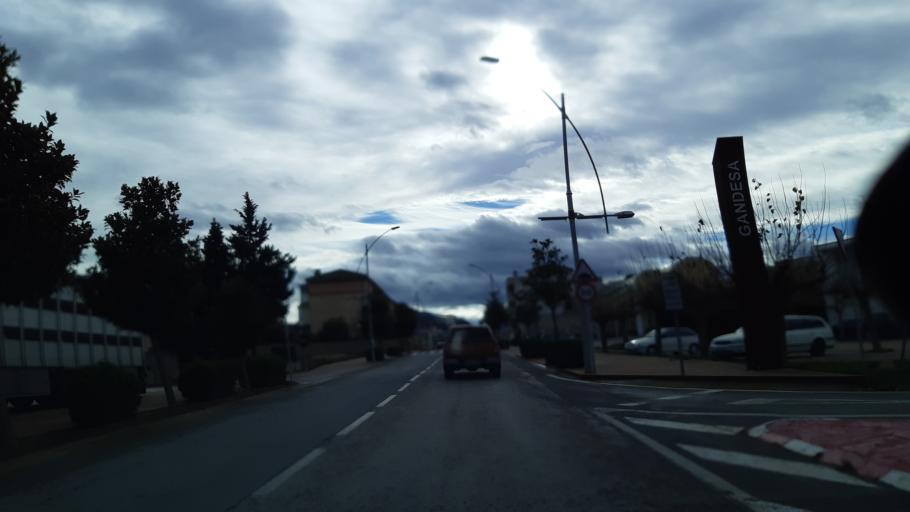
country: ES
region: Catalonia
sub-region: Provincia de Tarragona
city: Gandesa
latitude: 41.0583
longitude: 0.4414
